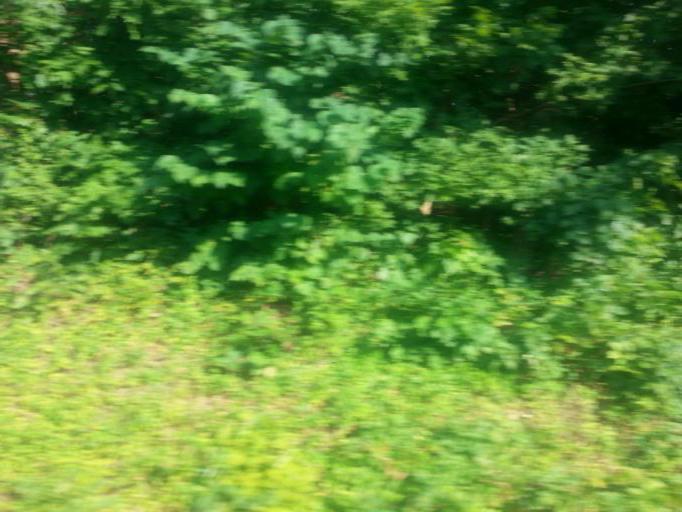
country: US
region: Tennessee
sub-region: Sevier County
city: Seymour
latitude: 35.8613
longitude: -83.7706
